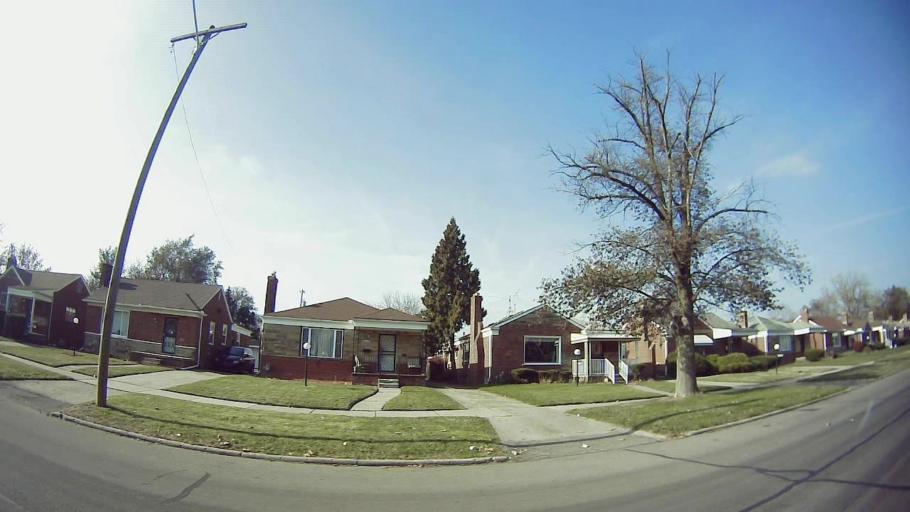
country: US
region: Michigan
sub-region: Oakland County
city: Oak Park
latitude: 42.4224
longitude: -83.1897
